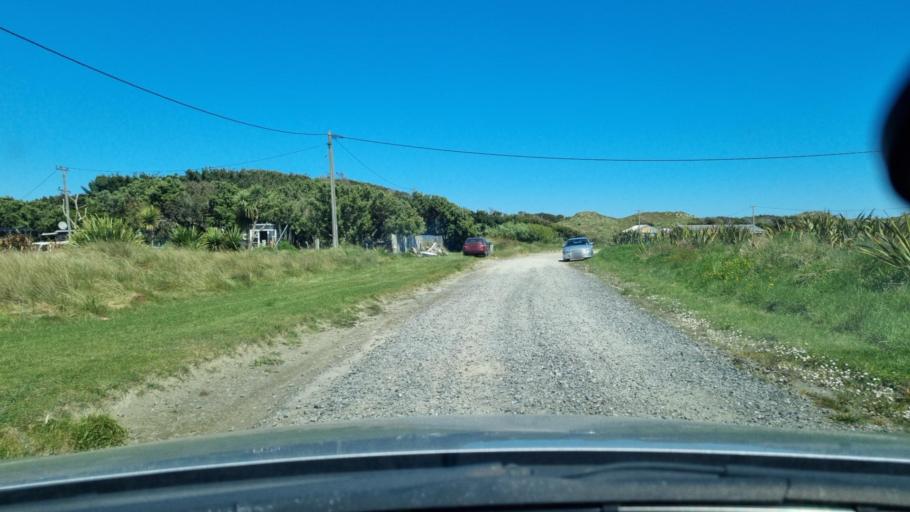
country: NZ
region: Southland
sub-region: Invercargill City
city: Invercargill
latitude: -46.4383
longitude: 168.2369
